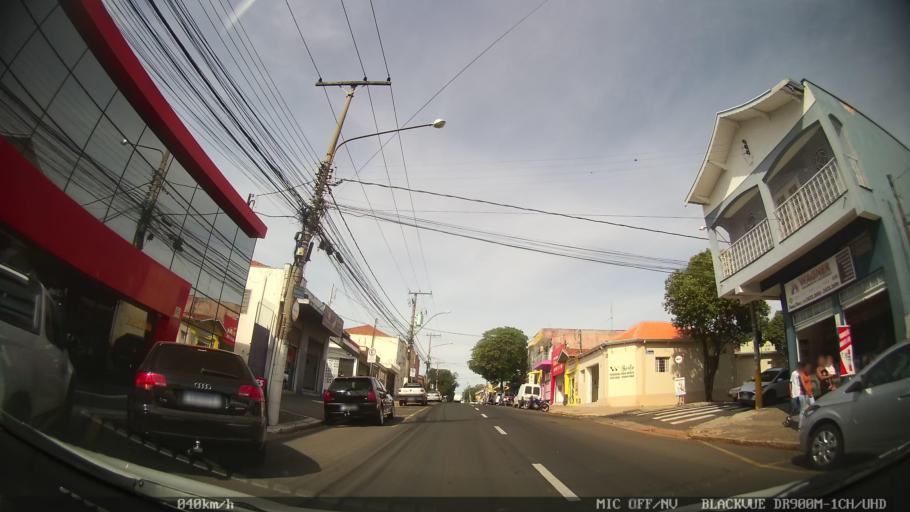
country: BR
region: Sao Paulo
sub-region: Piracicaba
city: Piracicaba
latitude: -22.7441
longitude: -47.6512
